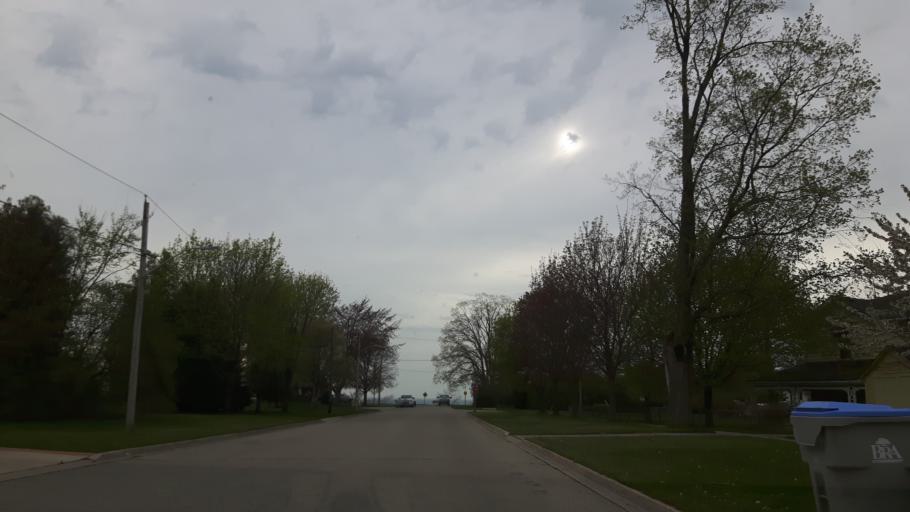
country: CA
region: Ontario
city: Goderich
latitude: 43.7406
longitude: -81.7229
